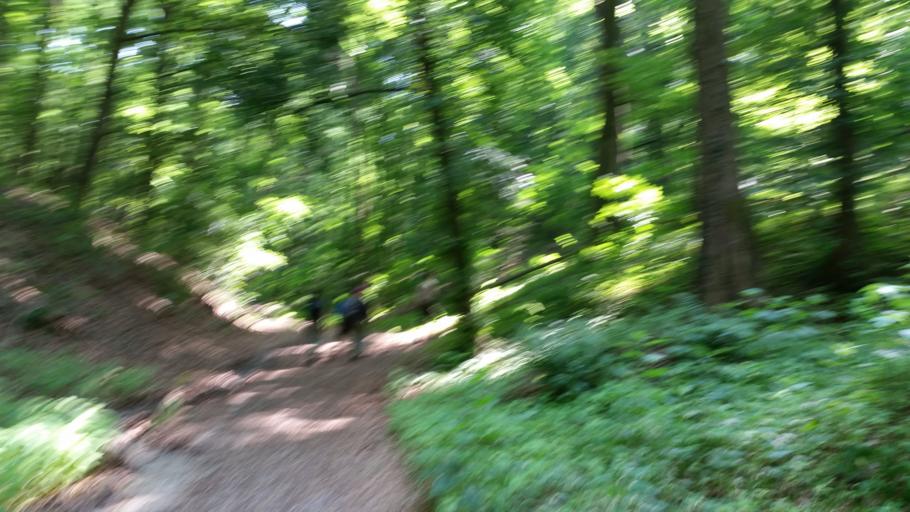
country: DE
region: Brandenburg
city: Reitwein
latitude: 52.4961
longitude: 14.5670
